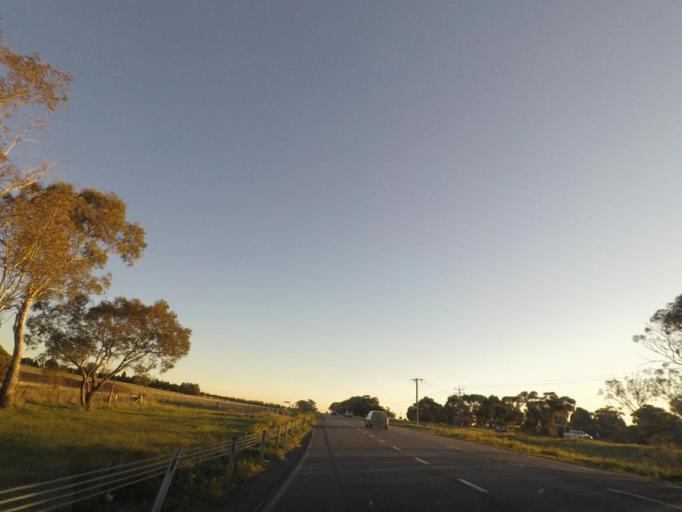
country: AU
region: Victoria
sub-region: Hume
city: Craigieburn
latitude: -37.4984
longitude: 144.9572
